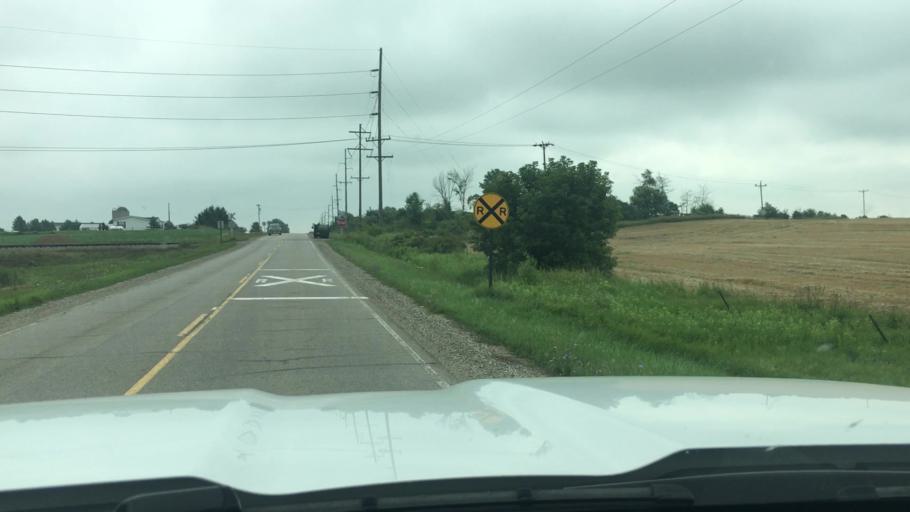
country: US
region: Michigan
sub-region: Sanilac County
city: Brown City
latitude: 43.2559
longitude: -83.0270
